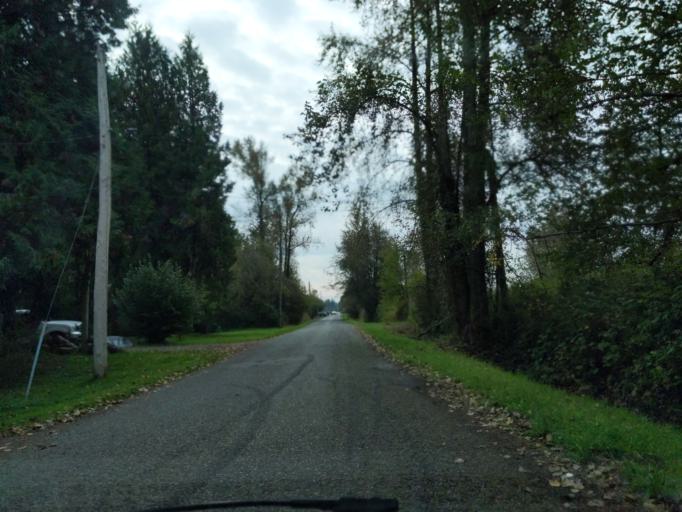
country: CA
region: British Columbia
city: Walnut Grove
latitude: 49.2000
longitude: -122.6443
